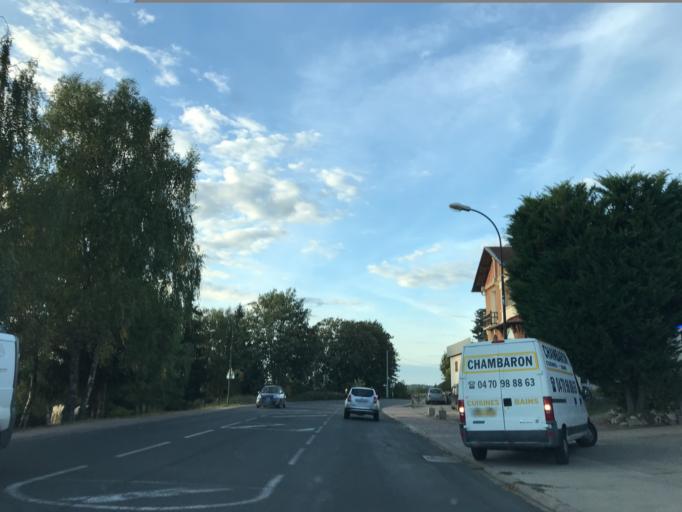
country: FR
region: Auvergne
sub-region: Departement de l'Allier
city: Abrest
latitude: 46.0997
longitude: 3.4442
